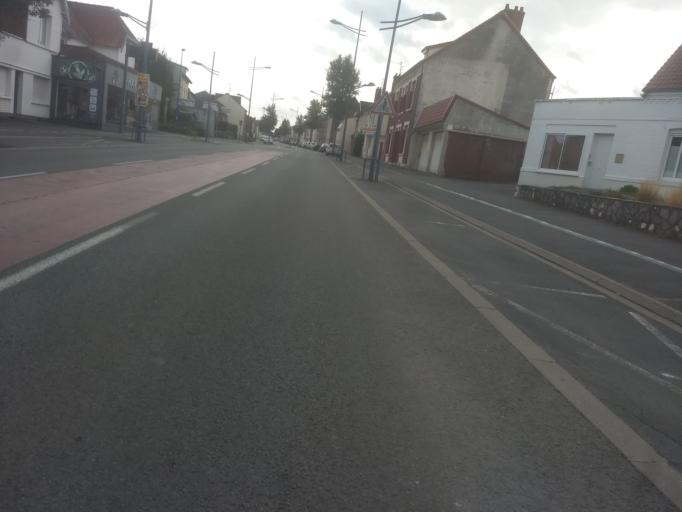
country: FR
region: Nord-Pas-de-Calais
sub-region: Departement du Pas-de-Calais
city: Beaurains
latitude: 50.2704
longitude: 2.7843
